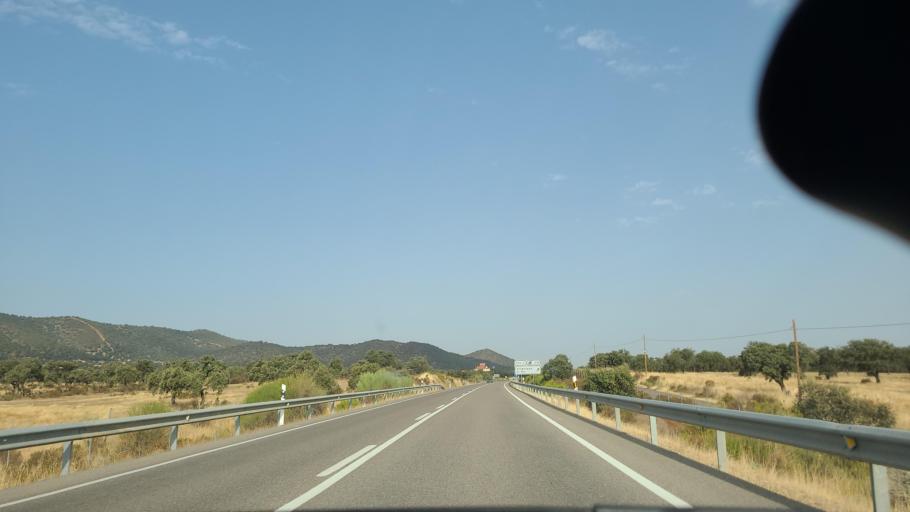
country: ES
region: Andalusia
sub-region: Province of Cordoba
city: Belmez
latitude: 38.2089
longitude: -5.1318
